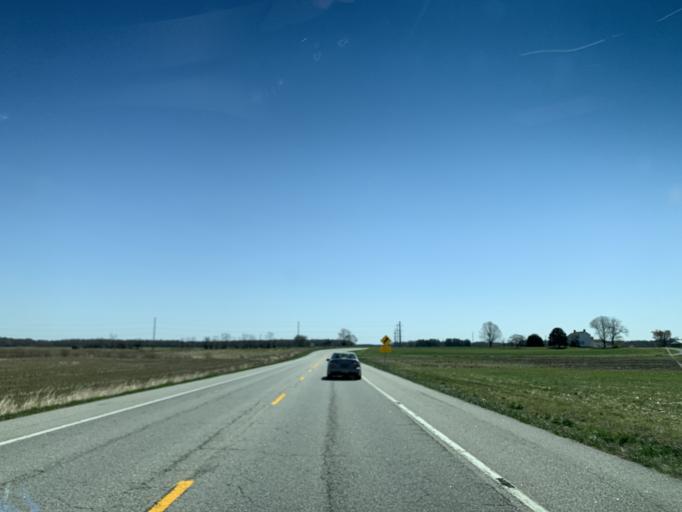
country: US
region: Maryland
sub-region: Queen Anne's County
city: Centreville
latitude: 38.9991
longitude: -76.0523
